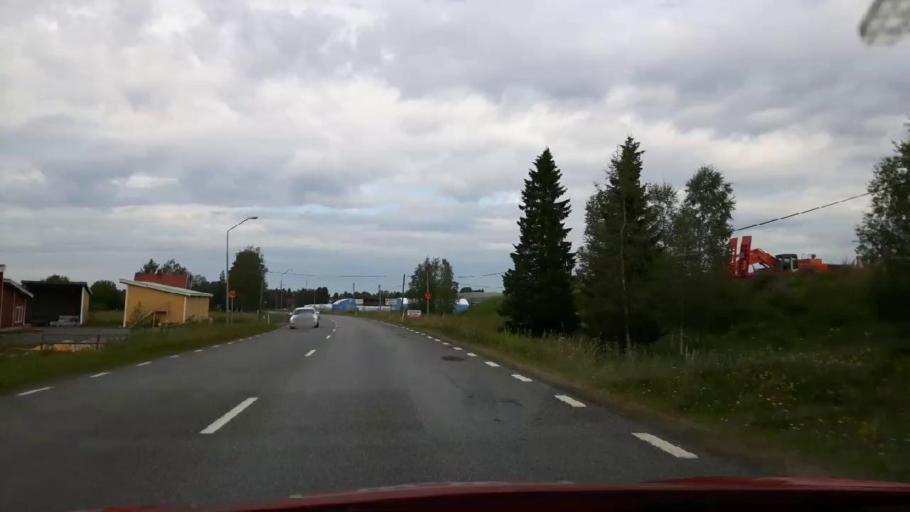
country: SE
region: Jaemtland
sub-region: Stroemsunds Kommun
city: Stroemsund
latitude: 63.5694
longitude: 15.3626
